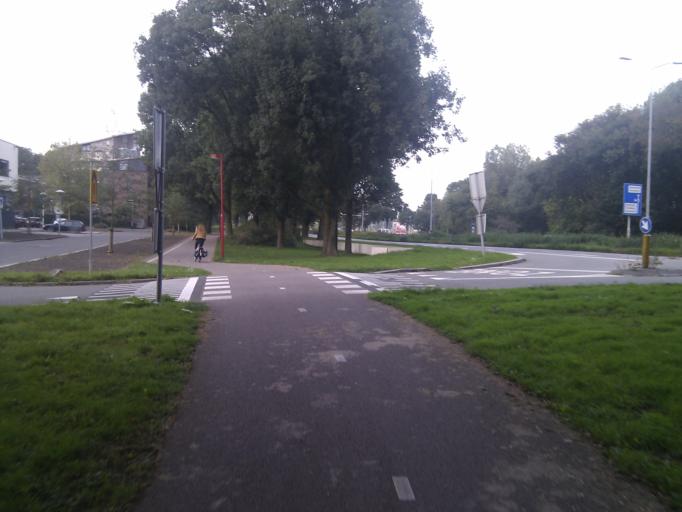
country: NL
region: Utrecht
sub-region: Gemeente Utrecht
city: Utrecht
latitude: 52.1000
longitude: 5.1426
